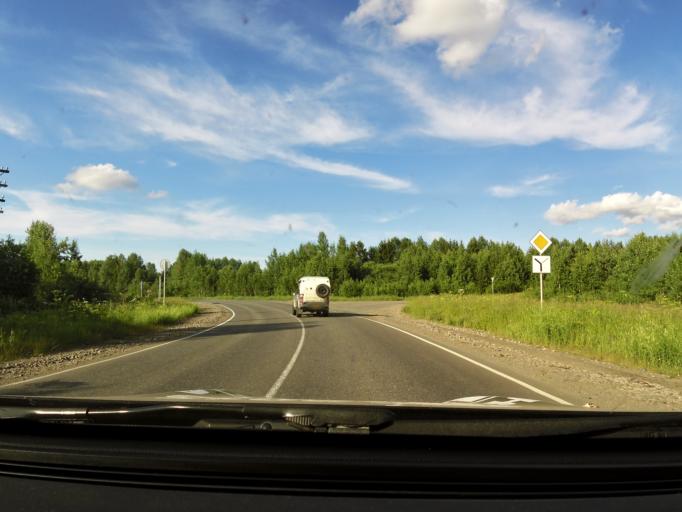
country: RU
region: Kirov
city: Belorechensk
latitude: 58.7170
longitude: 52.3342
